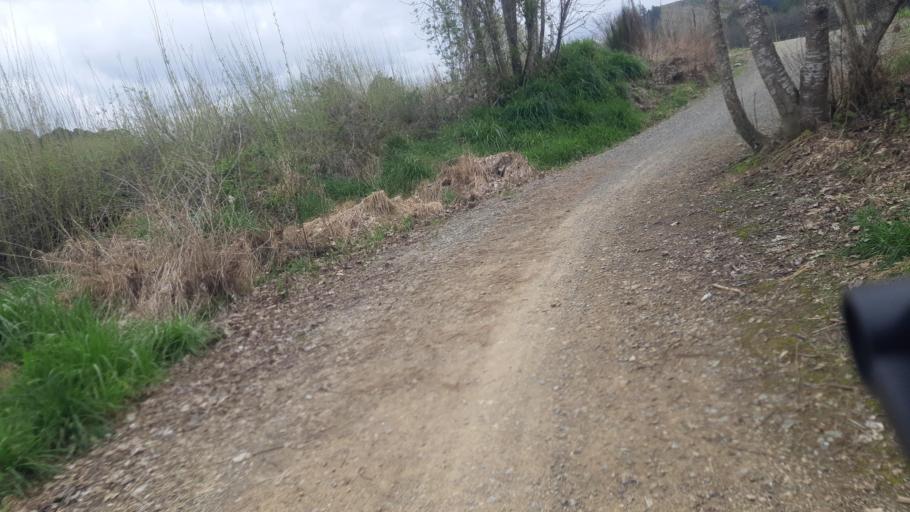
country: NZ
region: Tasman
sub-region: Tasman District
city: Wakefield
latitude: -41.4046
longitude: 173.0231
